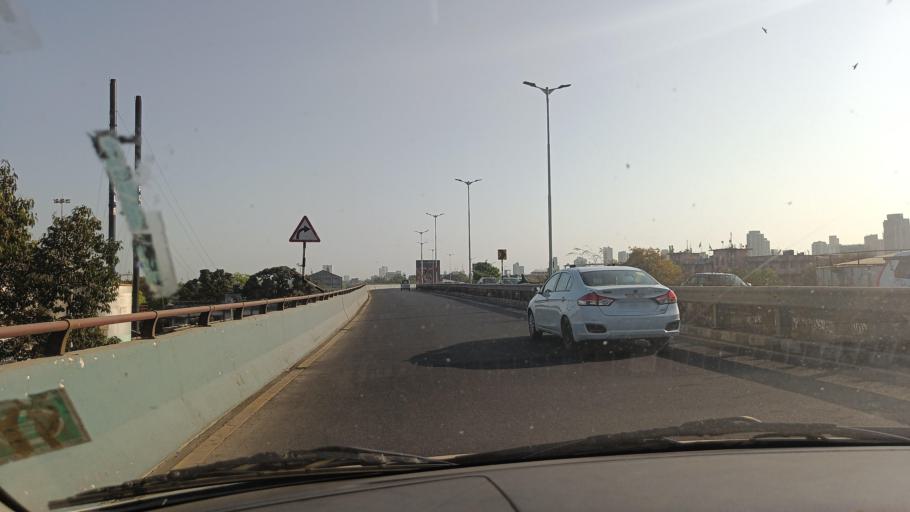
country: IN
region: Maharashtra
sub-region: Mumbai Suburban
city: Mumbai
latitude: 18.9619
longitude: 72.8446
